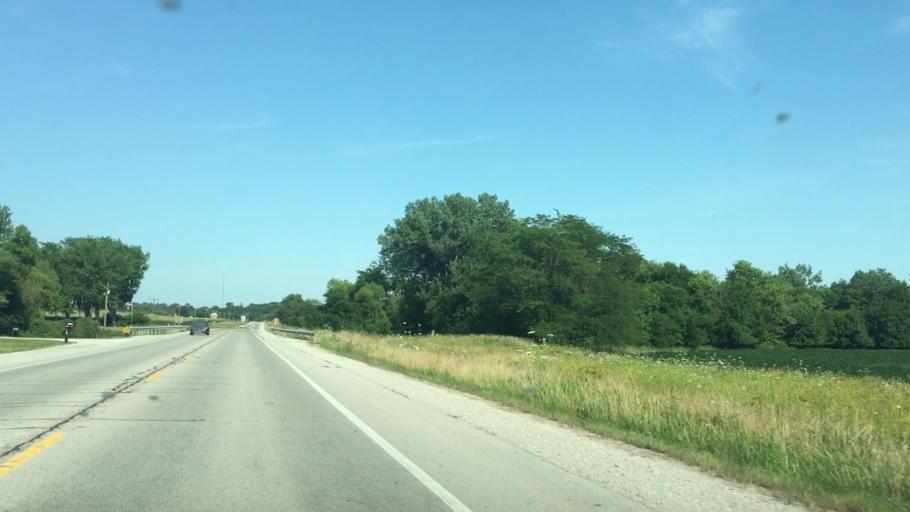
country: US
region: Iowa
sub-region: Johnson County
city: Tiffin
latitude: 41.7145
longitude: -91.7128
